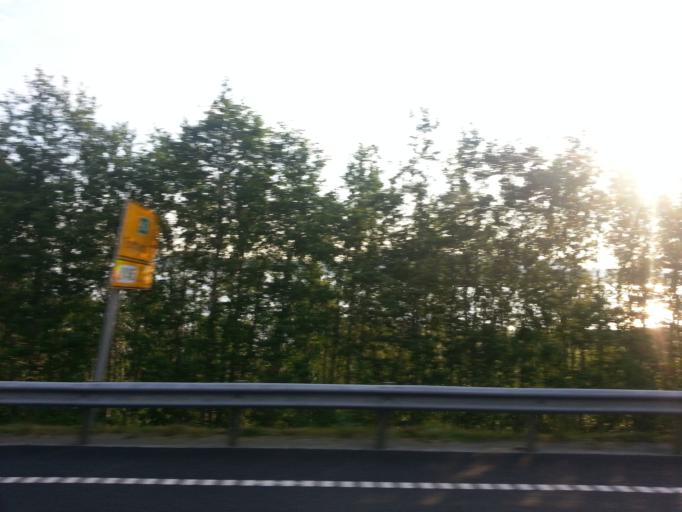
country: NO
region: Sor-Trondelag
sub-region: Malvik
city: Malvik
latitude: 63.4267
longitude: 10.7144
